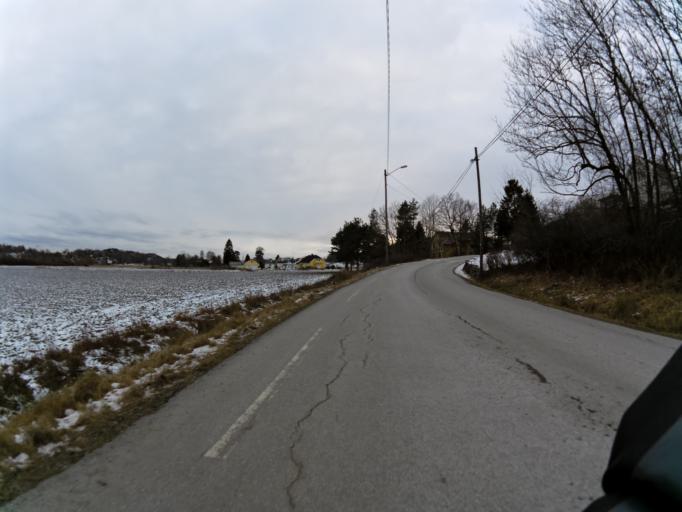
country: NO
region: Ostfold
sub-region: Fredrikstad
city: Fredrikstad
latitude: 59.2211
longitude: 10.8937
